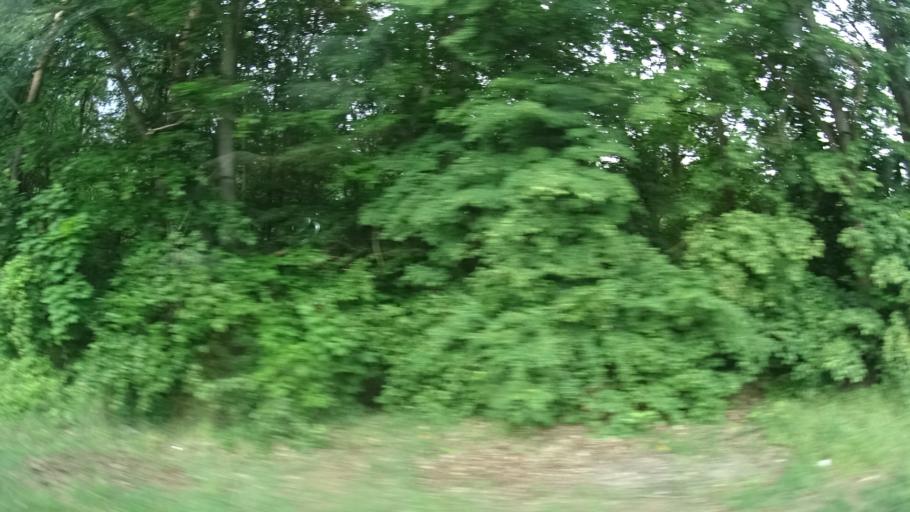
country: DE
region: Rheinland-Pfalz
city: Dudenhofen
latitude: 49.3236
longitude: 8.3847
